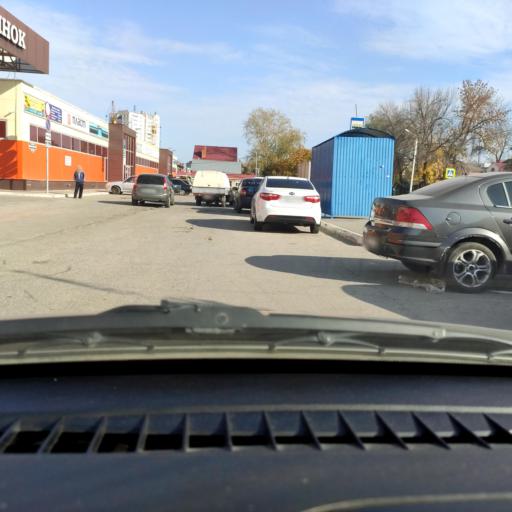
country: RU
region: Samara
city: Tol'yatti
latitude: 53.5177
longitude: 49.4106
